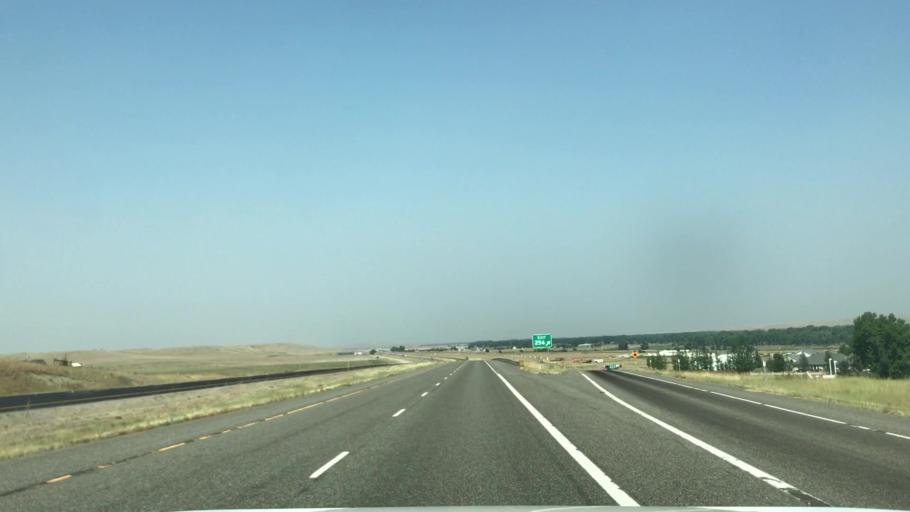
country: US
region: Montana
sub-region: Cascade County
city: Sun Prairie
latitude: 47.2772
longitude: -111.7040
